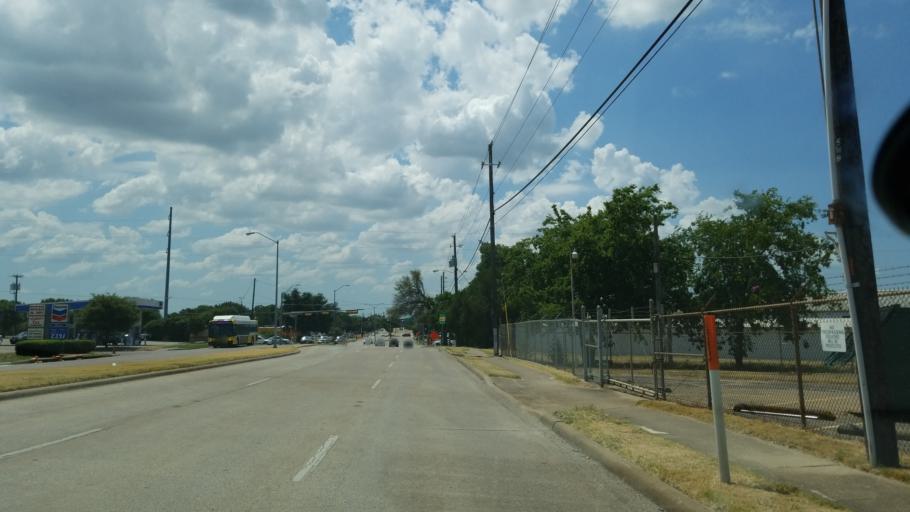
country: US
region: Texas
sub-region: Dallas County
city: Cockrell Hill
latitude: 32.7218
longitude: -96.8916
